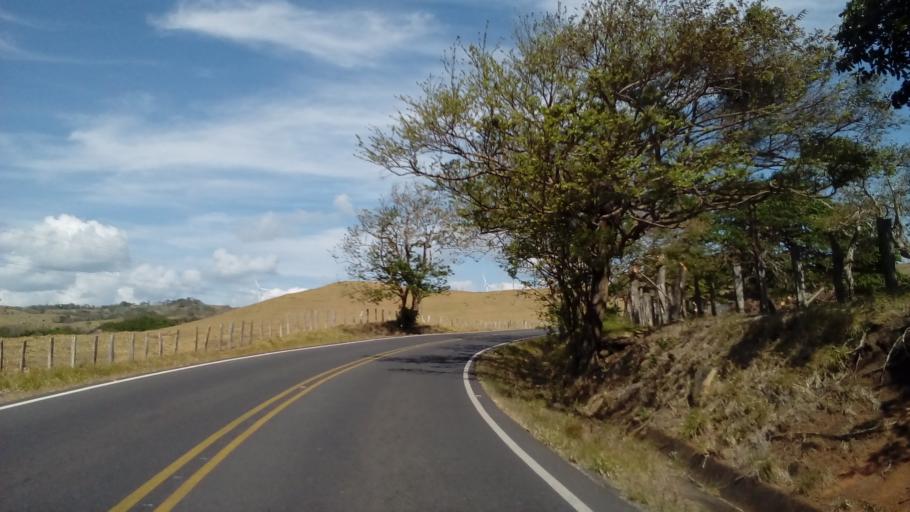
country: CR
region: Guanacaste
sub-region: Canton de Tilaran
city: Tilaran
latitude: 10.4920
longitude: -85.0154
